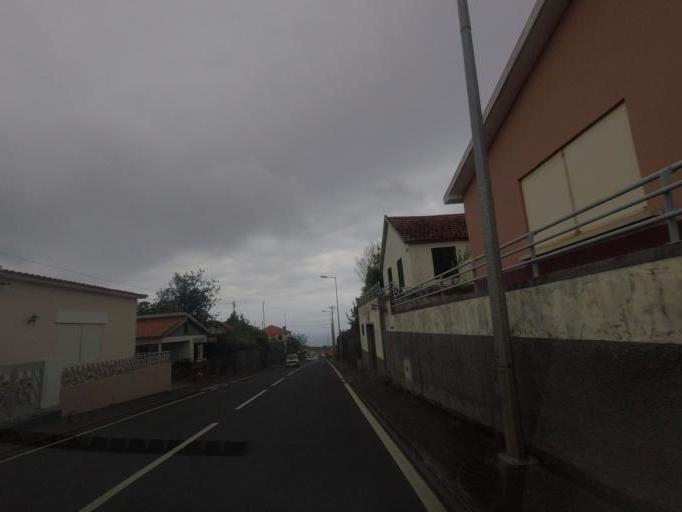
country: PT
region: Madeira
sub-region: Santana
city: Santana
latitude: 32.8192
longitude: -16.8876
